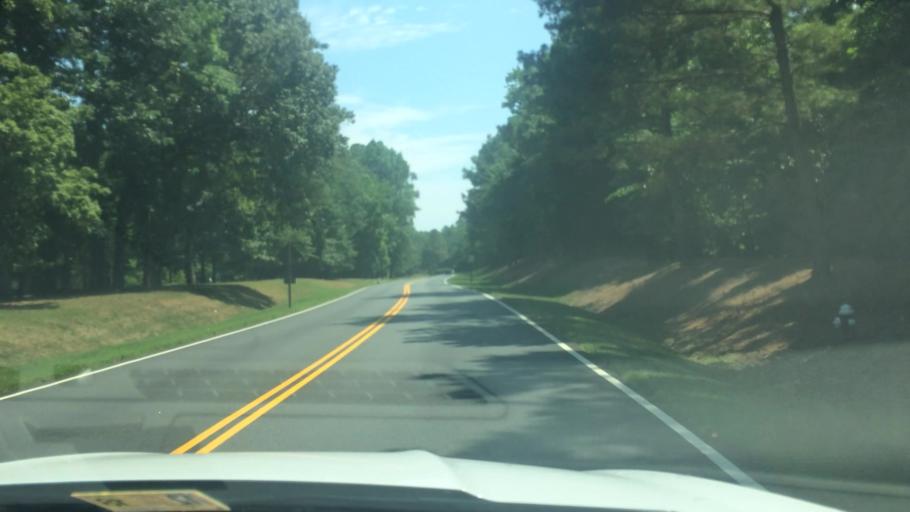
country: US
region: Virginia
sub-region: City of Williamsburg
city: Williamsburg
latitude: 37.2283
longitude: -76.6487
